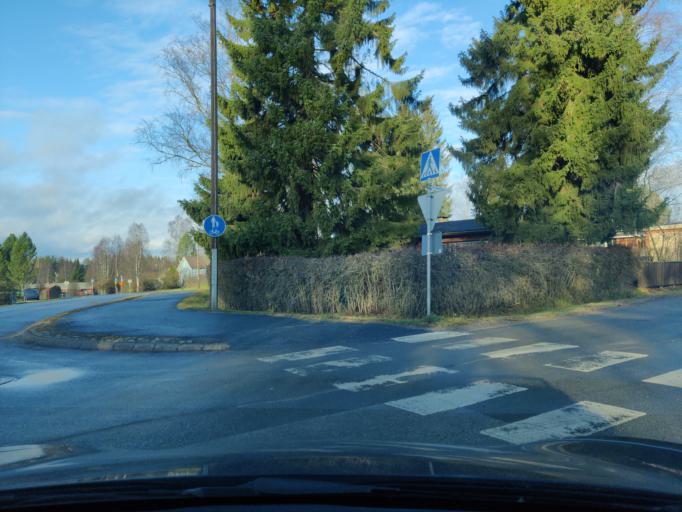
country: FI
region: Northern Savo
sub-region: Ylae-Savo
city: Kiuruvesi
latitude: 63.6456
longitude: 26.6268
